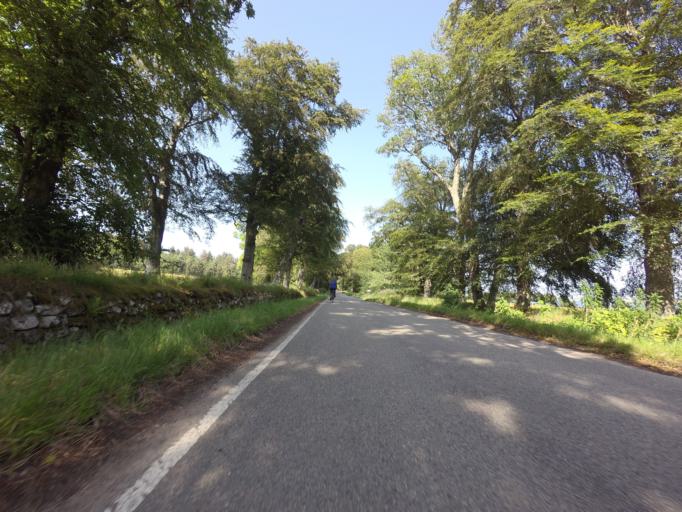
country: GB
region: Scotland
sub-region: Highland
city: Evanton
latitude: 57.6439
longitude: -4.3557
